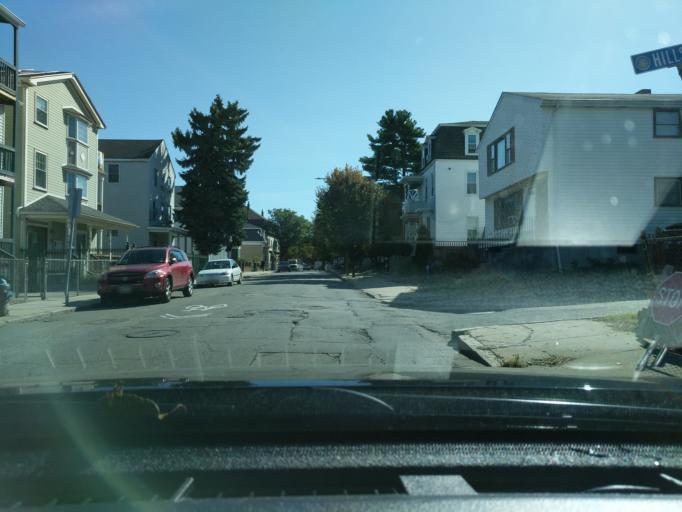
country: US
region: Massachusetts
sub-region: Middlesex County
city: Somerville
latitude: 42.3850
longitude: -71.0856
